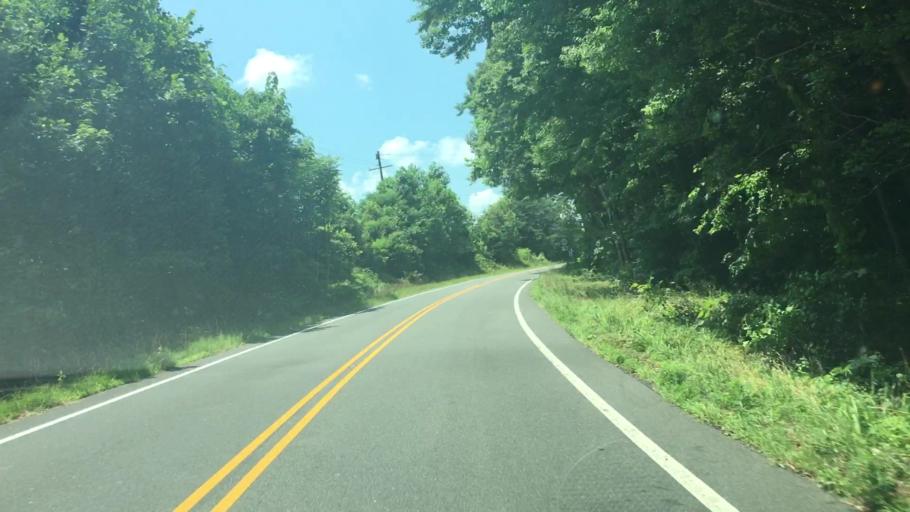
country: US
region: Virginia
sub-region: King George County
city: Passapatanzy
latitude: 38.2960
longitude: -77.3054
